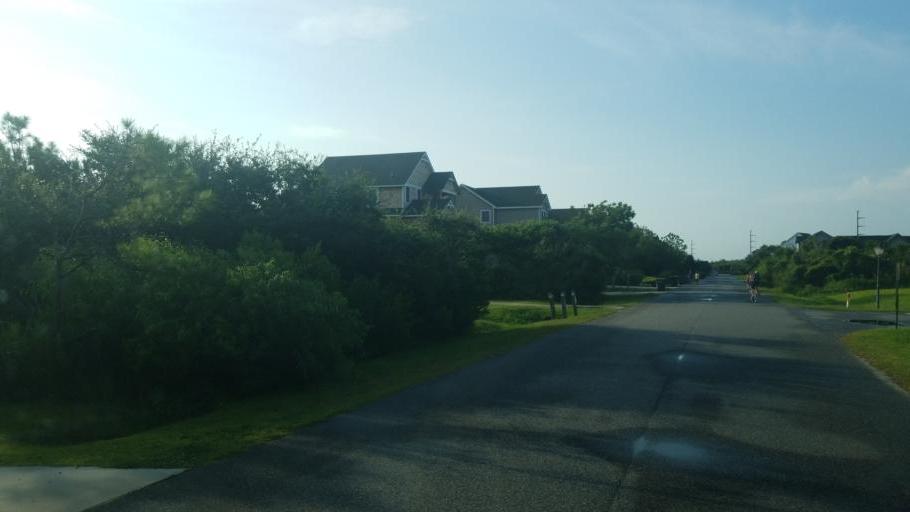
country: US
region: North Carolina
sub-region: Dare County
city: Nags Head
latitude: 35.9704
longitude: -75.6332
